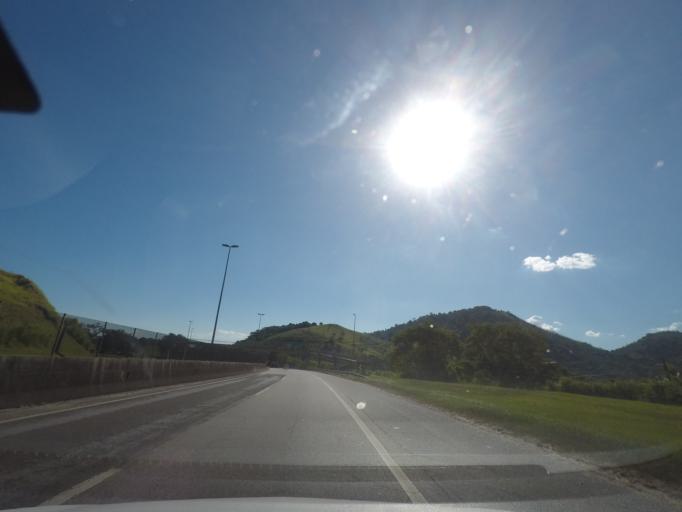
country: BR
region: Rio de Janeiro
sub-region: Guapimirim
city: Guapimirim
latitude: -22.6547
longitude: -43.0862
